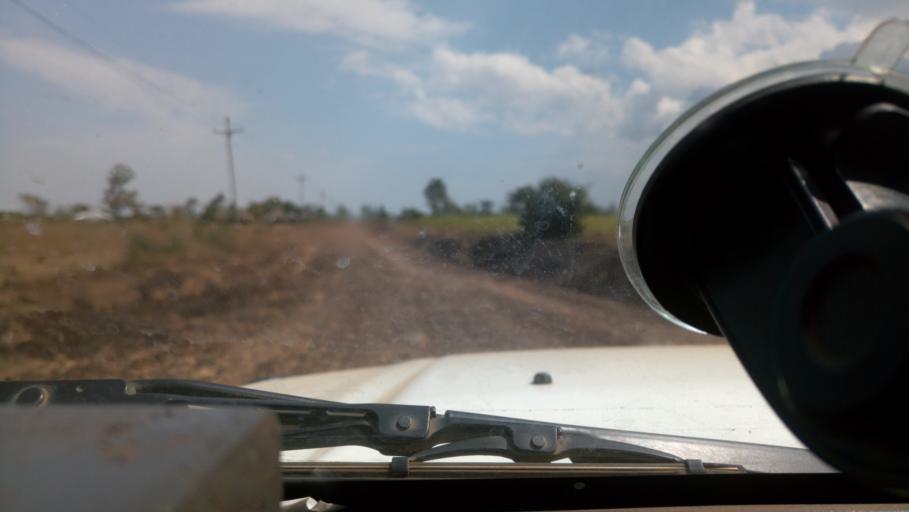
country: KE
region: Migori
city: Migori
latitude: -0.8562
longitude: 34.2939
